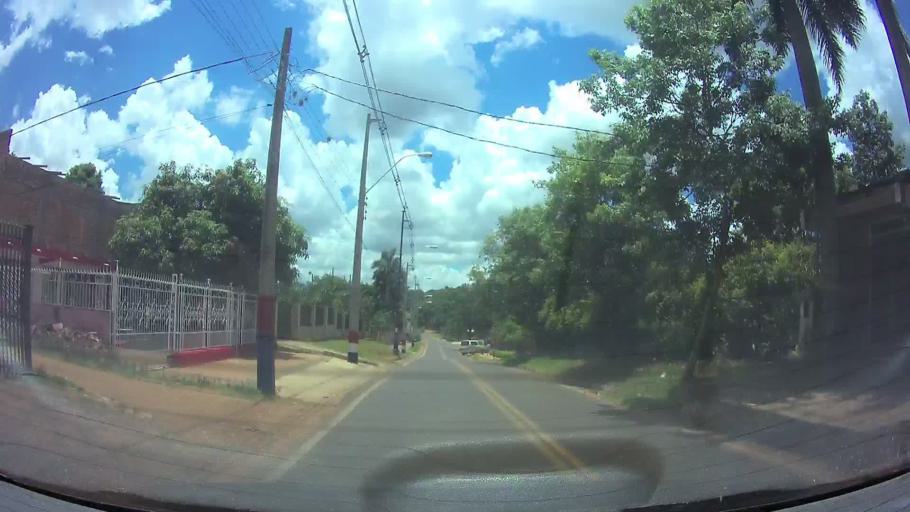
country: PY
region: Central
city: Capiata
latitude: -25.3098
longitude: -57.4336
